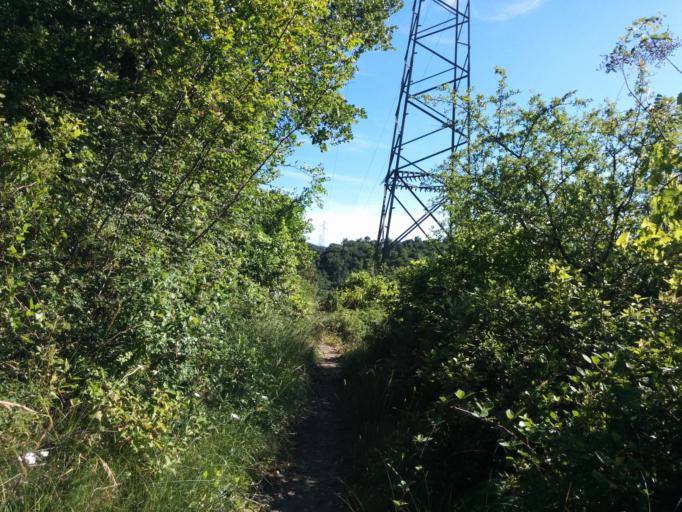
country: FR
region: Languedoc-Roussillon
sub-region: Departement du Gard
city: Bagard
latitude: 44.0938
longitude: 4.0552
